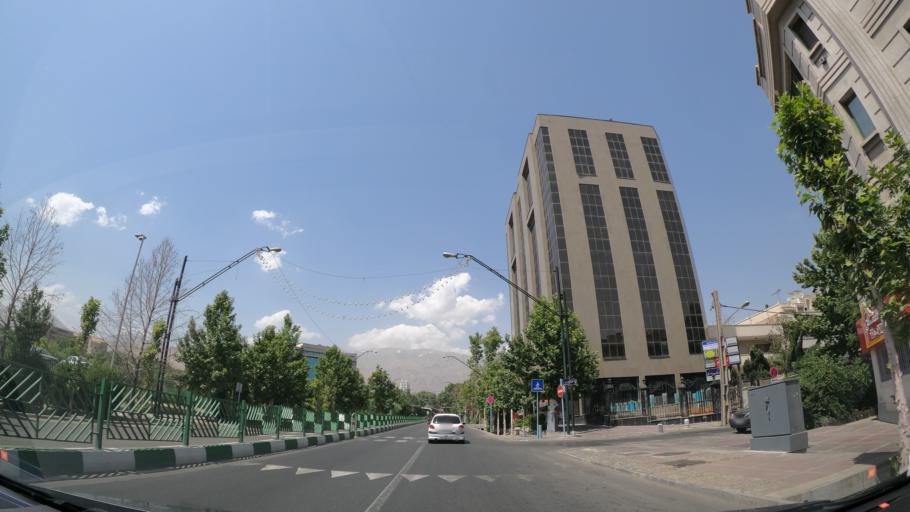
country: IR
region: Tehran
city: Tajrish
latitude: 35.7843
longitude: 51.4149
